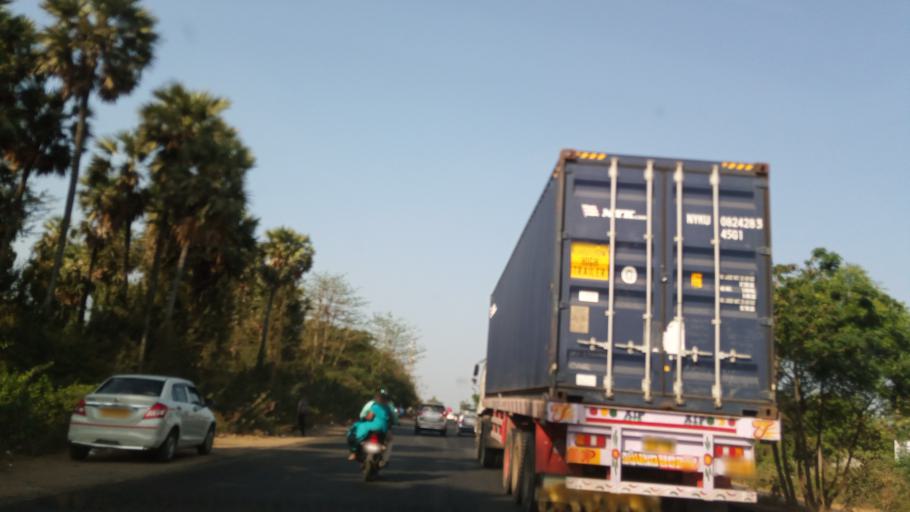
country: IN
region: Tamil Nadu
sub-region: Kancheepuram
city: Nandambakkam
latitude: 13.0271
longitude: 80.0278
